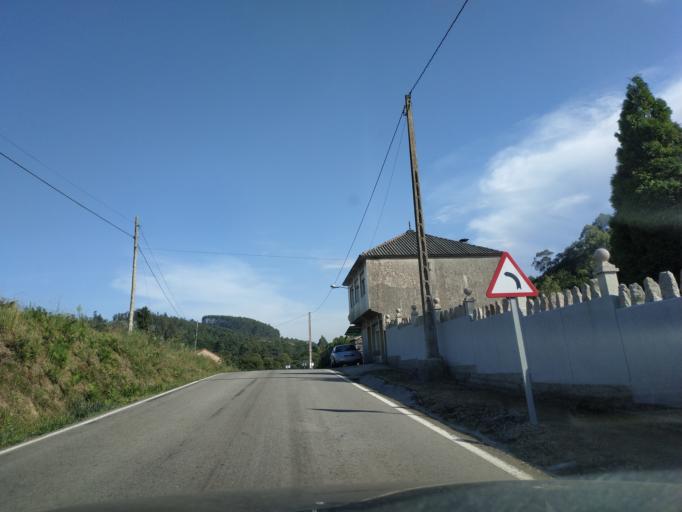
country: ES
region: Galicia
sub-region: Provincia da Coruna
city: Cerceda
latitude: 43.2332
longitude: -8.4799
